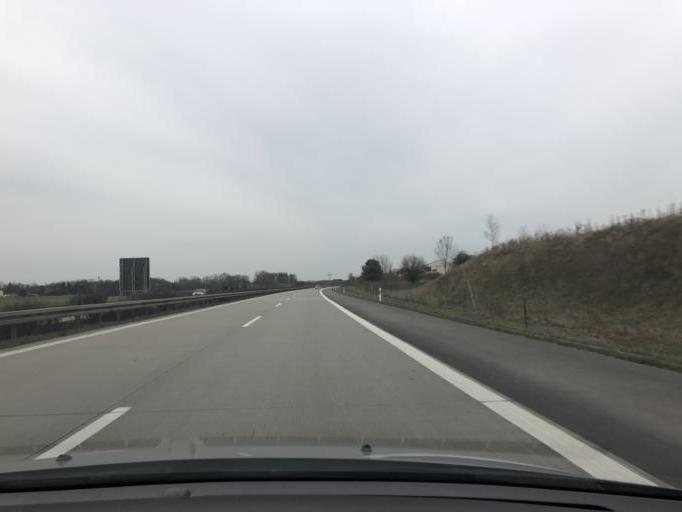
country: DE
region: Brandenburg
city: Wittstock
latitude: 53.1612
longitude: 12.4477
